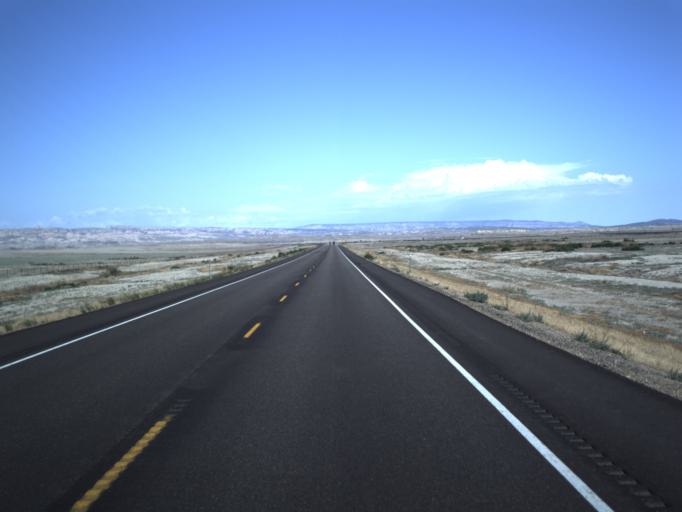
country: US
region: Utah
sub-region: Carbon County
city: East Carbon City
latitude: 38.9938
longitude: -110.2549
